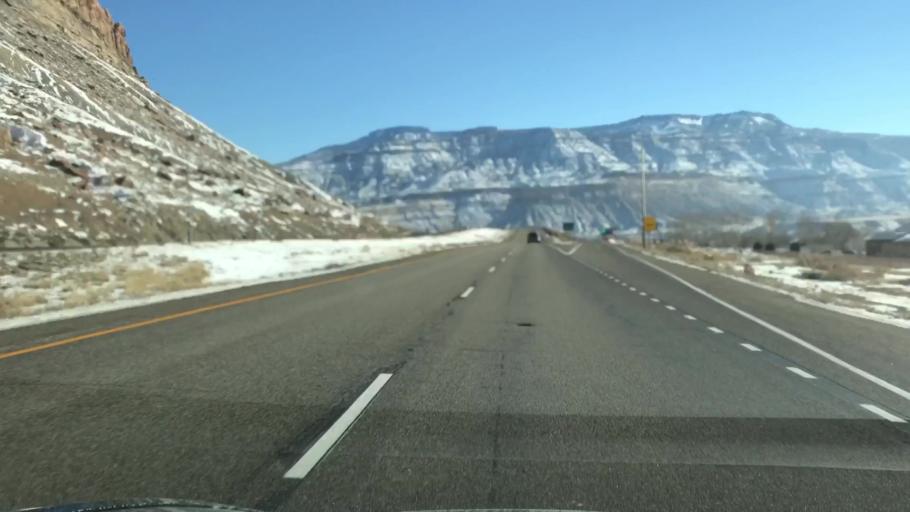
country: US
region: Colorado
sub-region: Mesa County
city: Palisade
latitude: 39.1194
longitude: -108.3644
